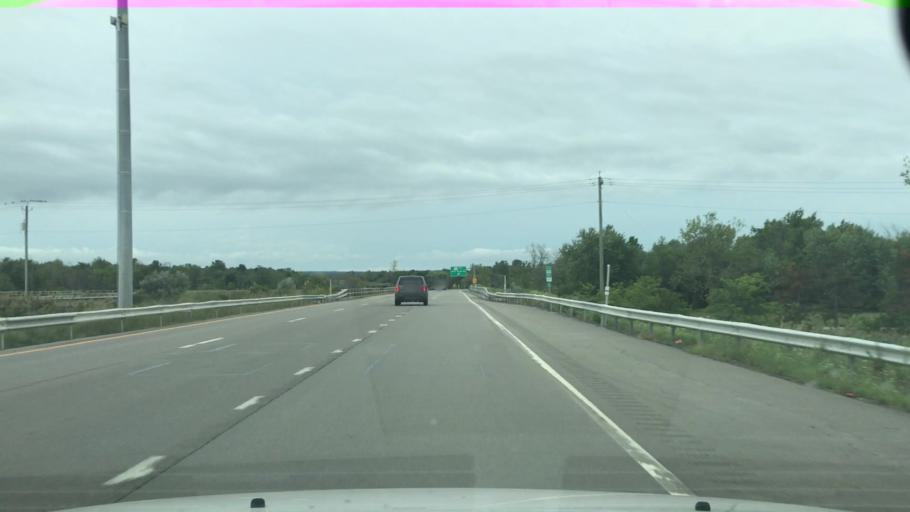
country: US
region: New York
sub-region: Erie County
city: Orchard Park
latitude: 42.7902
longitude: -78.7754
